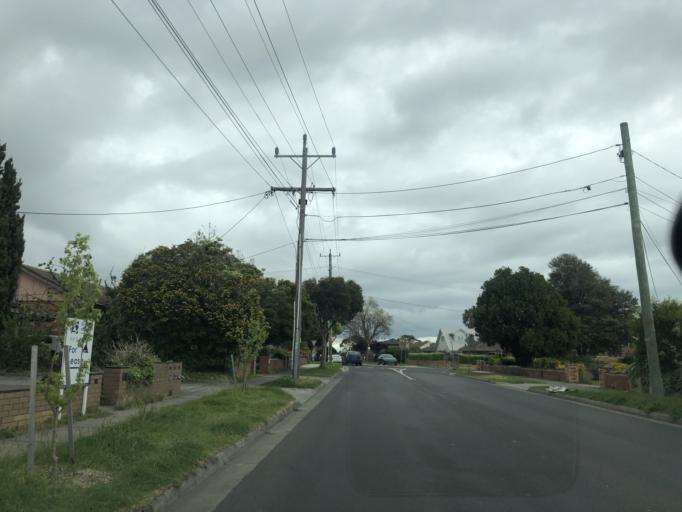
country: AU
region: Victoria
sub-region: Greater Dandenong
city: Dandenong
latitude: -37.9761
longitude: 145.2023
